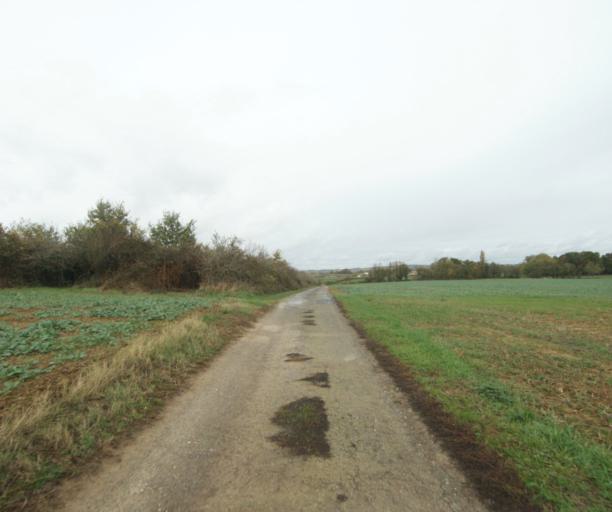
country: FR
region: Rhone-Alpes
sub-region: Departement de l'Ain
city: Pont-de-Vaux
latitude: 46.4570
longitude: 4.8808
